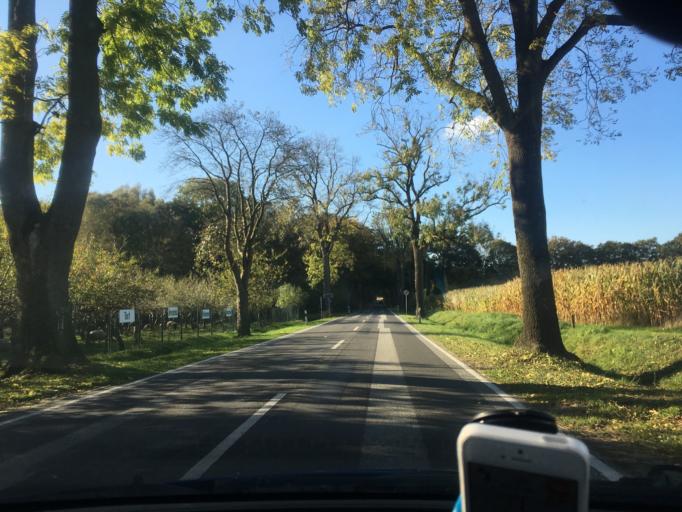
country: DE
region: Mecklenburg-Vorpommern
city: Zarrentin
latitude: 53.5263
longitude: 10.9787
